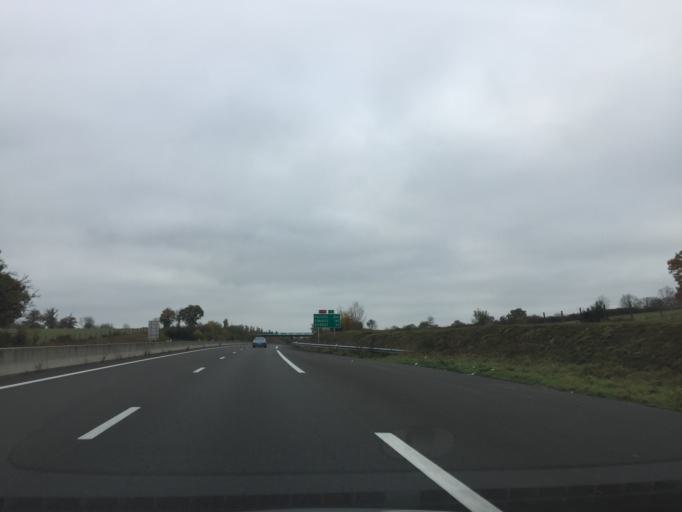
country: FR
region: Auvergne
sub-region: Departement de l'Allier
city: Huriel
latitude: 46.2994
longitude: 2.4363
